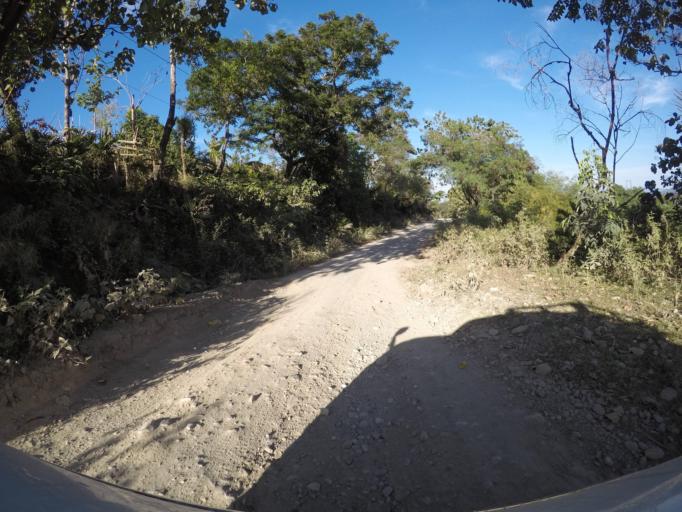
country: TL
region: Viqueque
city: Viqueque
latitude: -8.8681
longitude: 126.3308
